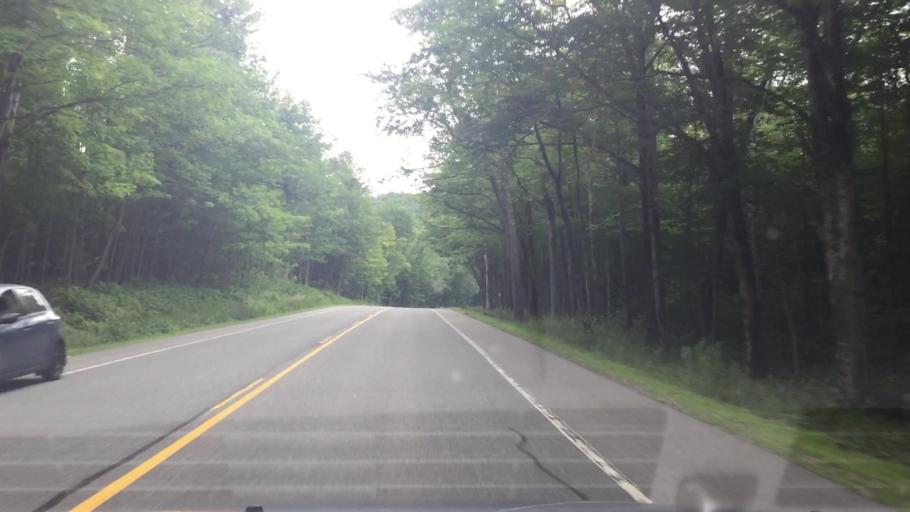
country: US
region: New Hampshire
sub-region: Grafton County
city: Deerfield
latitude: 44.2158
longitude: -71.6761
